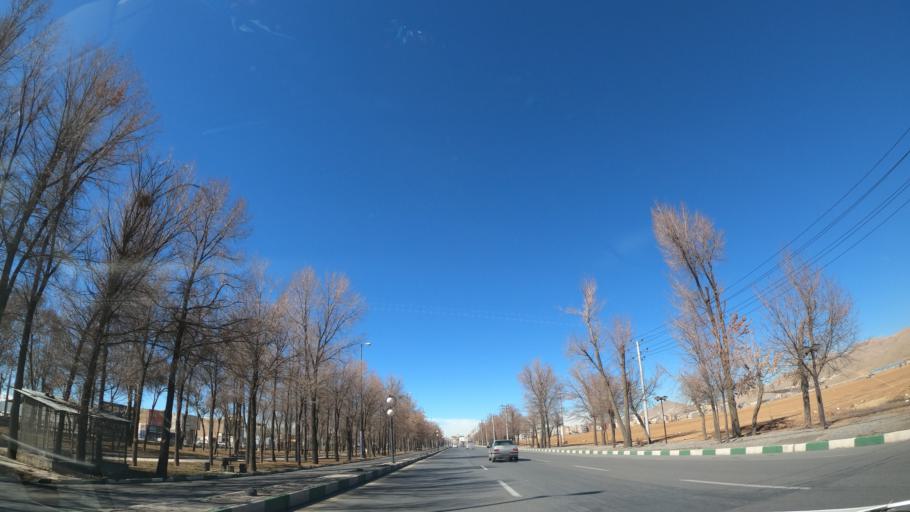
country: IR
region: Chahar Mahall va Bakhtiari
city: Shahrekord
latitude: 32.3089
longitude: 50.8969
